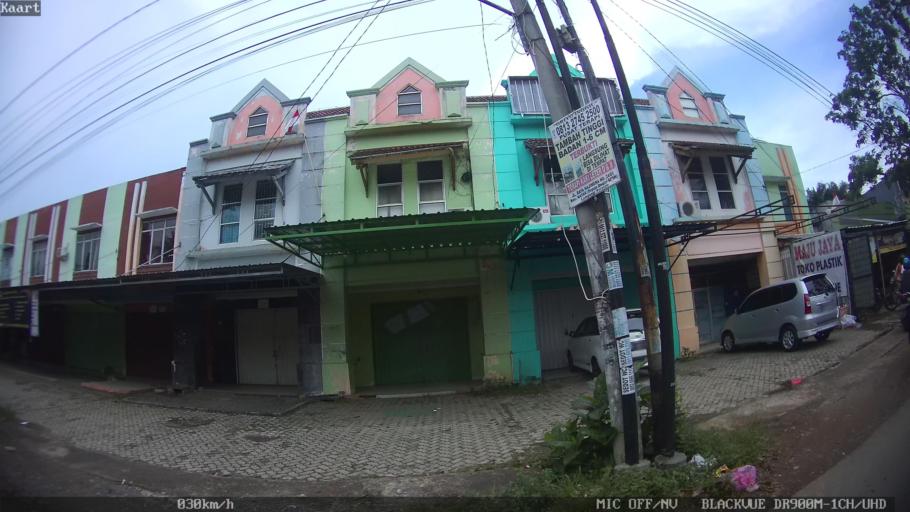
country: ID
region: Lampung
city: Kedaton
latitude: -5.3879
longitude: 105.2101
